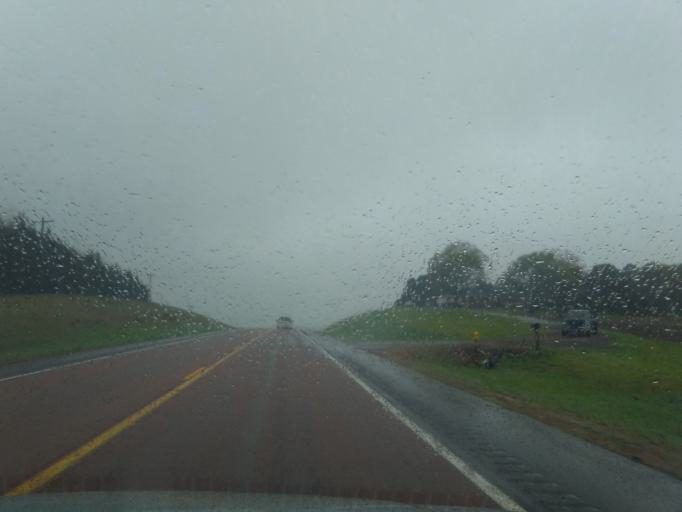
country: US
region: Nebraska
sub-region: Wayne County
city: Wayne
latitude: 42.2355
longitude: -97.1555
